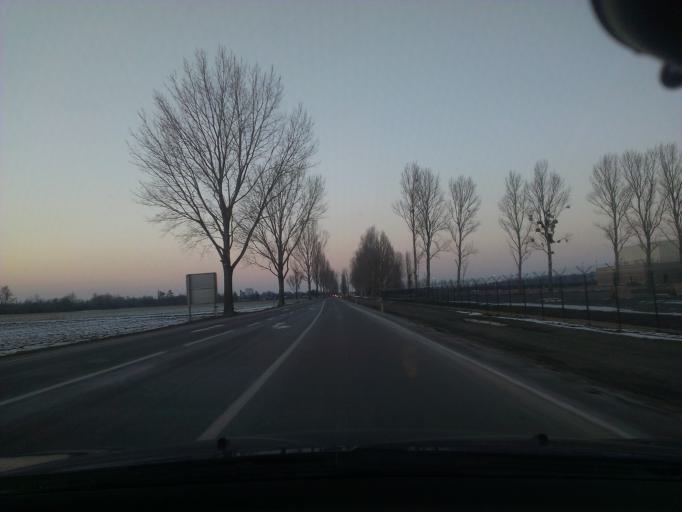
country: AT
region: Lower Austria
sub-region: Politischer Bezirk Bruck an der Leitha
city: Enzersdorf an der Fischa
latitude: 48.0674
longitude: 16.6098
